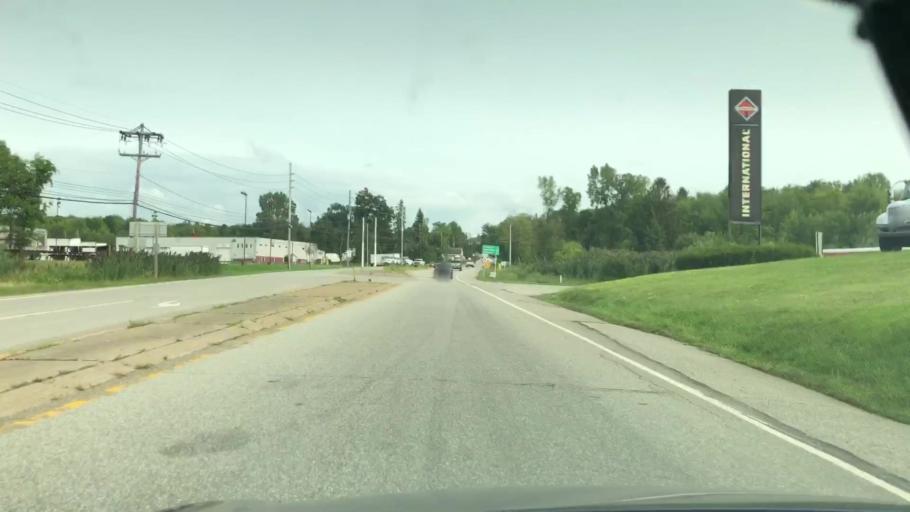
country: US
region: Pennsylvania
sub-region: Erie County
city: Wesleyville
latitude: 42.0923
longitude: -80.0043
